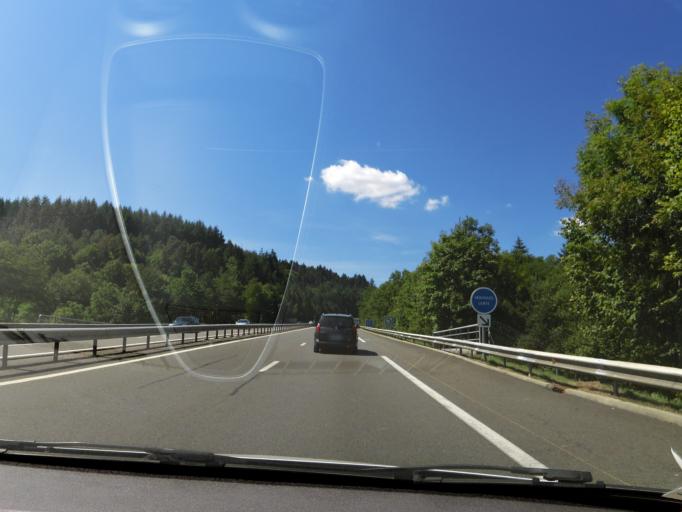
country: FR
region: Rhone-Alpes
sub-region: Departement de la Loire
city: Noiretable
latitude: 45.8523
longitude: 3.7860
